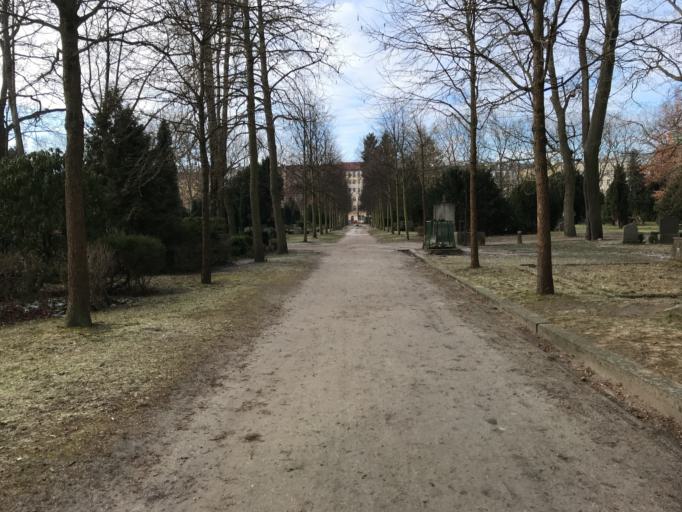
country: DE
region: Berlin
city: Friedrichshain Bezirk
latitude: 52.5208
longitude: 13.4414
